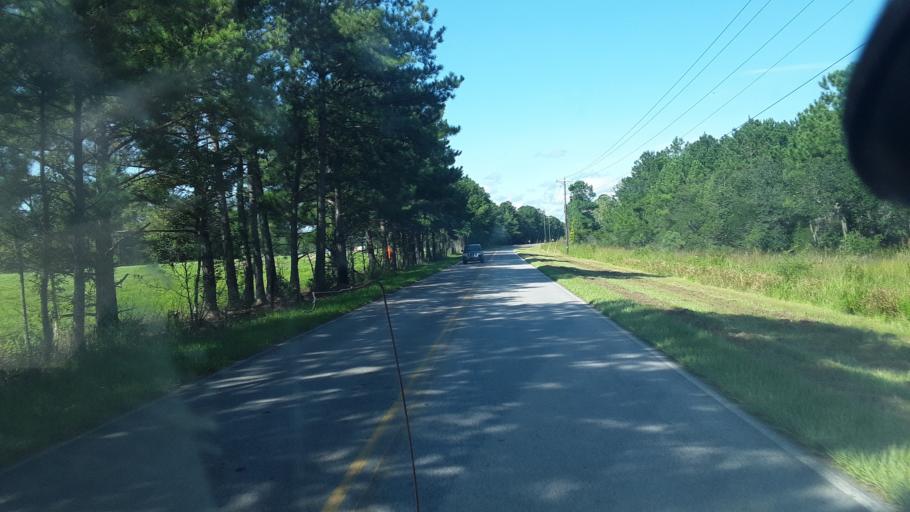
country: US
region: South Carolina
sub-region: Hampton County
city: Yemassee
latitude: 32.5937
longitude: -80.9172
